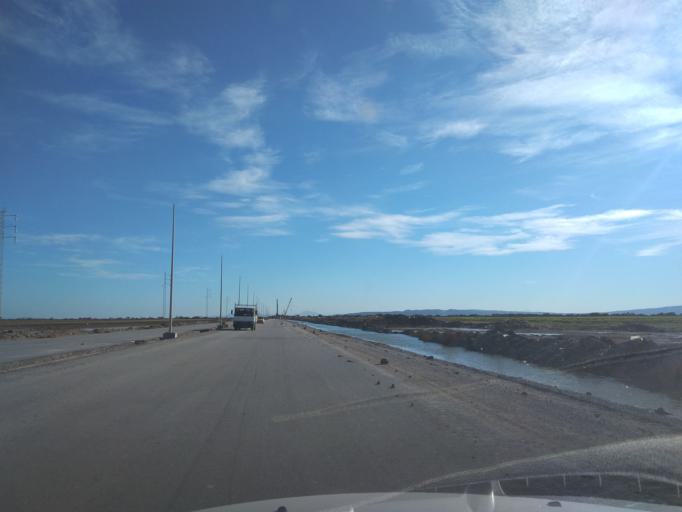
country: TN
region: Ariana
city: Qal'at al Andalus
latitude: 37.0299
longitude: 10.1368
